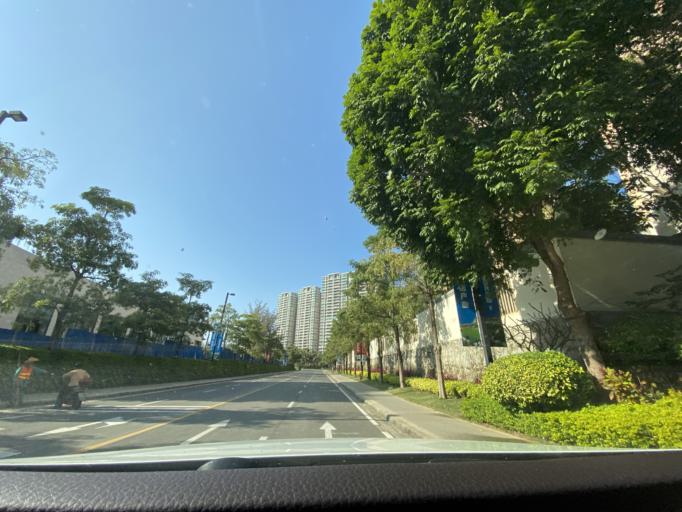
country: CN
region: Hainan
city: Yingzhou
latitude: 18.4108
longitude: 109.8866
